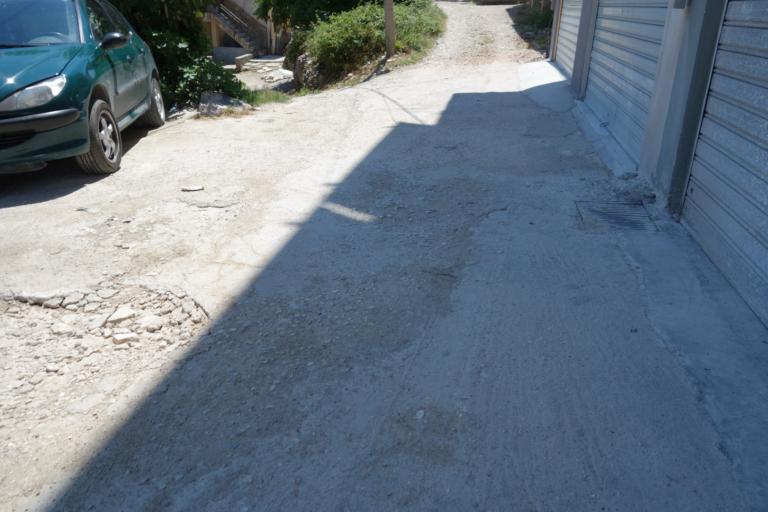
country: AL
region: Gjirokaster
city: Gjirokaster
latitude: 40.0807
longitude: 20.1312
